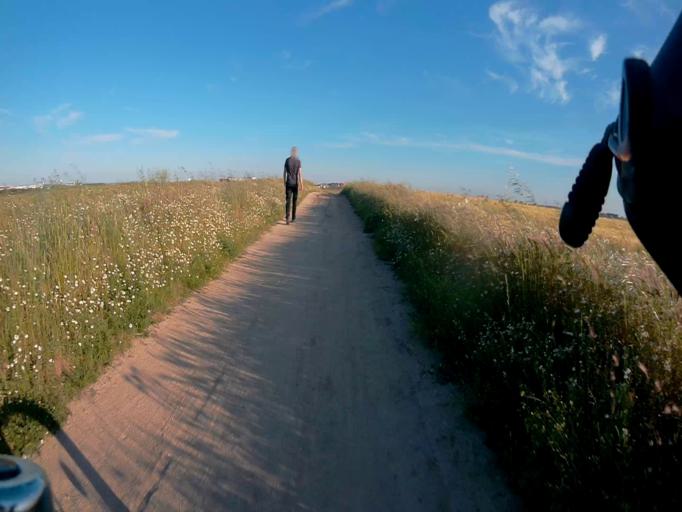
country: ES
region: Madrid
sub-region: Provincia de Madrid
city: Alcorcon
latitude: 40.3184
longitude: -3.8120
